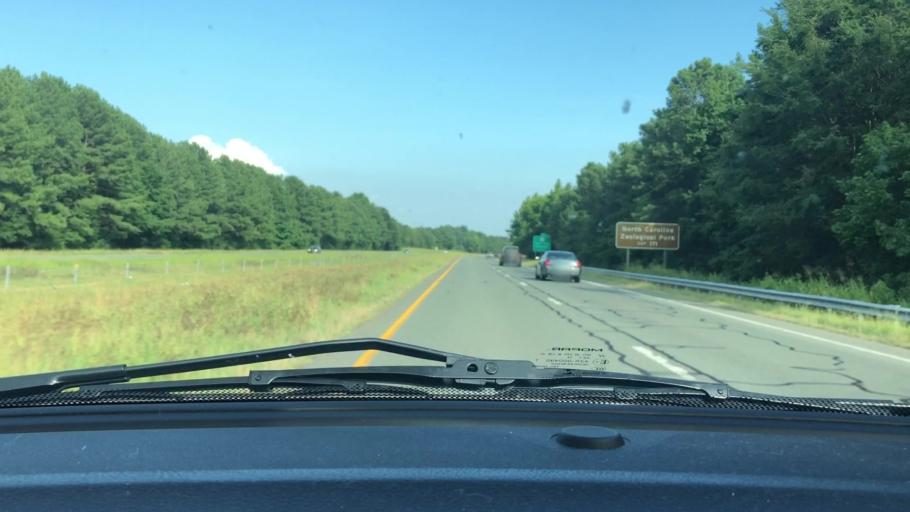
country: US
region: North Carolina
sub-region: Chatham County
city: Siler City
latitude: 35.7457
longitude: -79.4419
